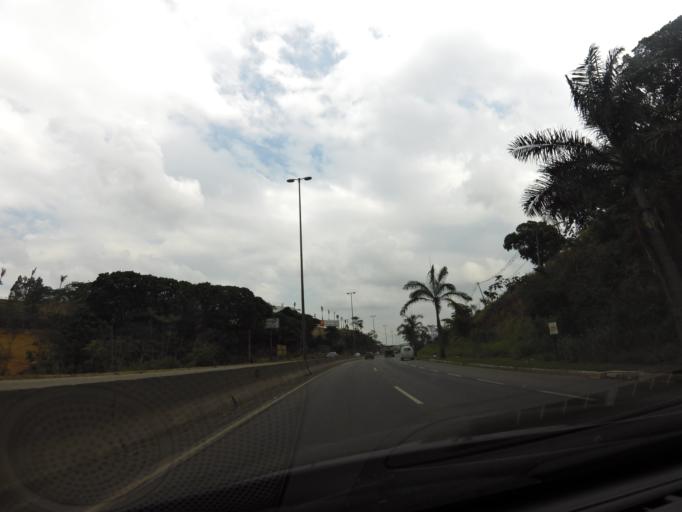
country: BR
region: Espirito Santo
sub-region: Vitoria
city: Vitoria
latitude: -20.3510
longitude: -40.4131
